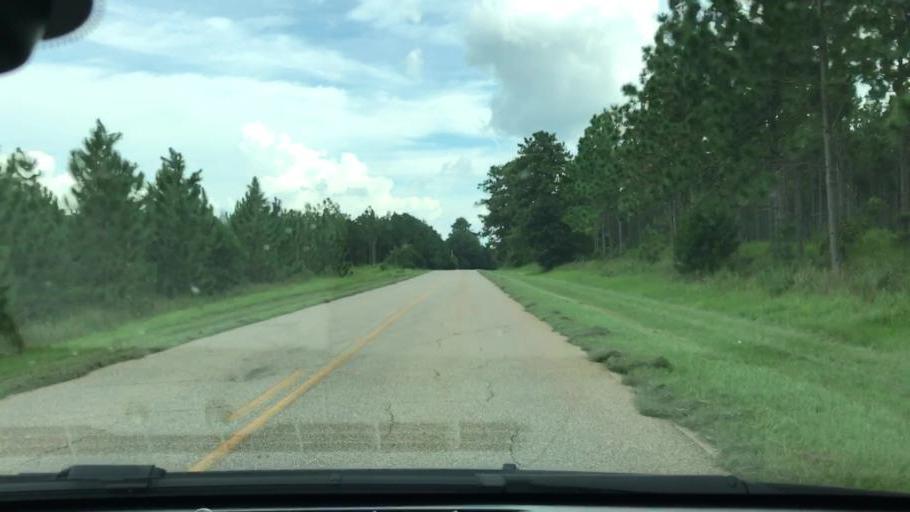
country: US
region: Georgia
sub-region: Clay County
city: Fort Gaines
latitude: 31.5607
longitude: -84.9817
